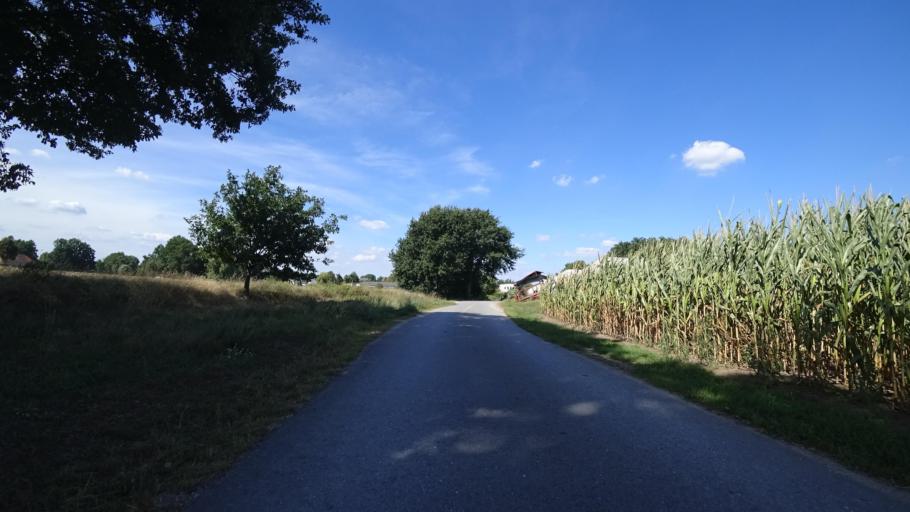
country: DE
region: North Rhine-Westphalia
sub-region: Regierungsbezirk Detmold
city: Guetersloh
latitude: 51.8851
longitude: 8.4061
